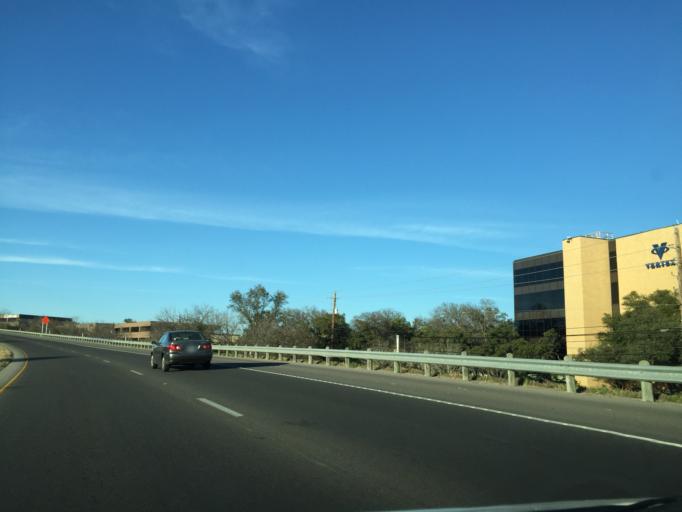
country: US
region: Texas
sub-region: Travis County
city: Rollingwood
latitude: 30.2728
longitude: -97.8175
